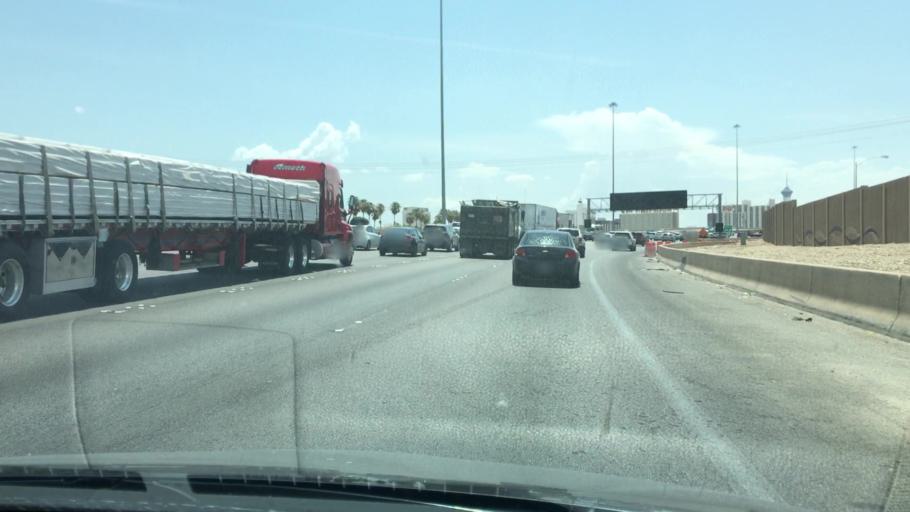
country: US
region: Nevada
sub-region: Clark County
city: Las Vegas
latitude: 36.1844
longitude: -115.1440
